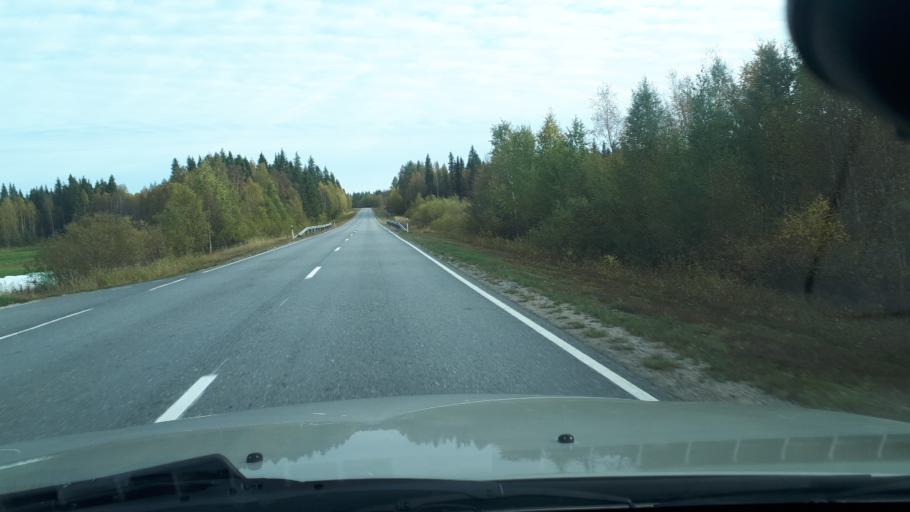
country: FI
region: Lapland
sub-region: Rovaniemi
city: Rovaniemi
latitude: 65.9558
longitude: 25.9331
